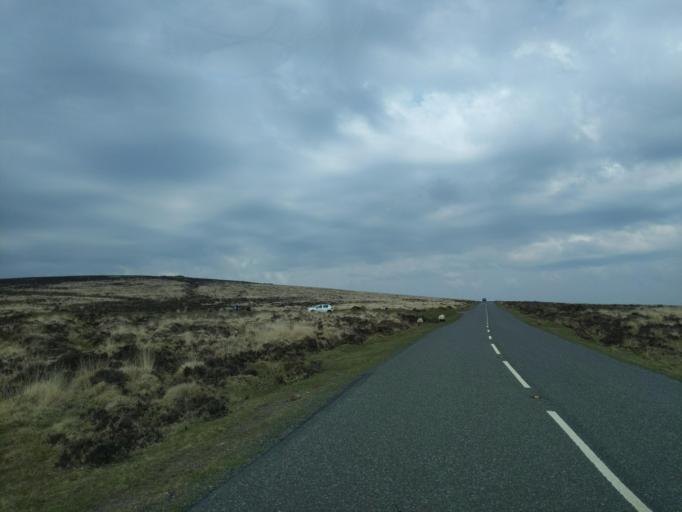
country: GB
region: England
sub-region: Devon
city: Ashburton
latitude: 50.6093
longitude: -3.8843
